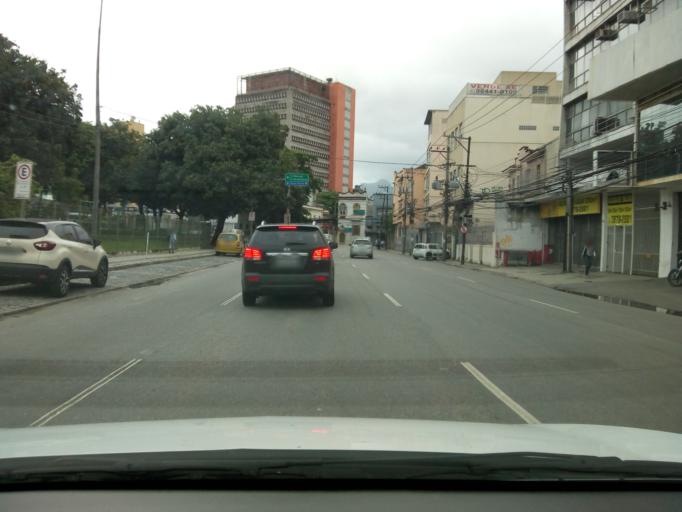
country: BR
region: Rio de Janeiro
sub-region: Rio De Janeiro
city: Rio de Janeiro
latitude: -22.8980
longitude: -43.2226
